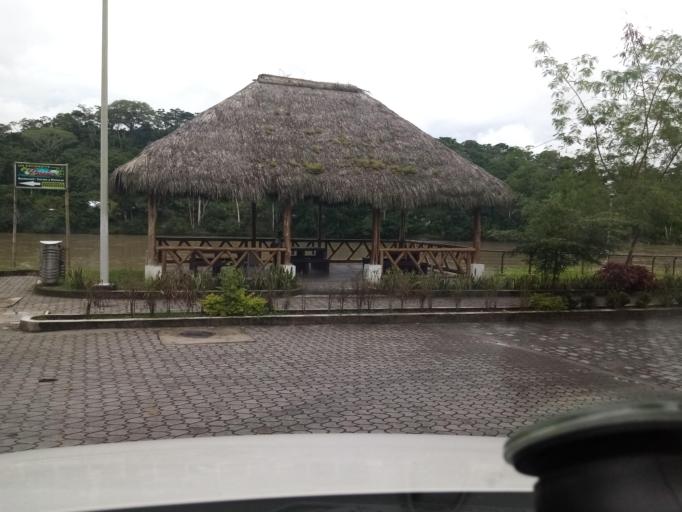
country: EC
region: Napo
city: Tena
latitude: -1.0431
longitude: -77.7925
